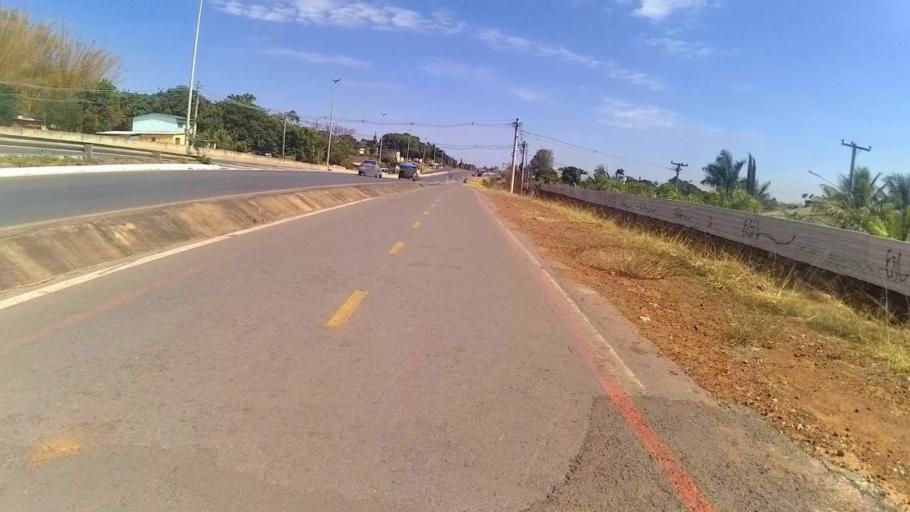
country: BR
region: Federal District
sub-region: Brasilia
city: Brasilia
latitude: -15.6646
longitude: -47.8419
